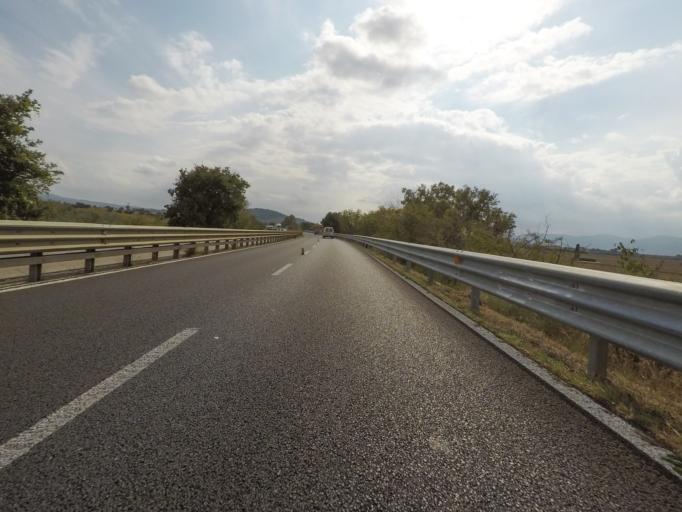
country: IT
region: Tuscany
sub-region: Provincia di Grosseto
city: Grosseto
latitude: 42.7231
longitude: 11.1379
